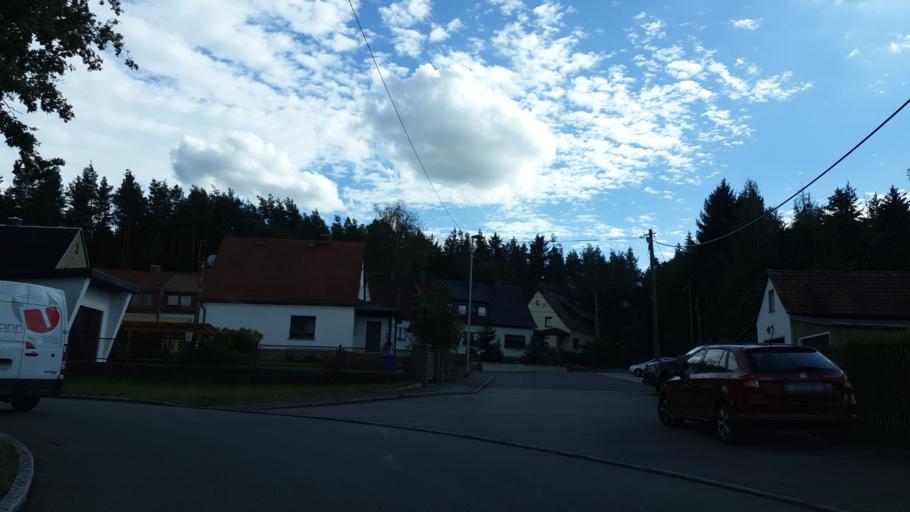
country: DE
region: Saxony
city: Lichtenstein
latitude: 50.7077
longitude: 12.6387
